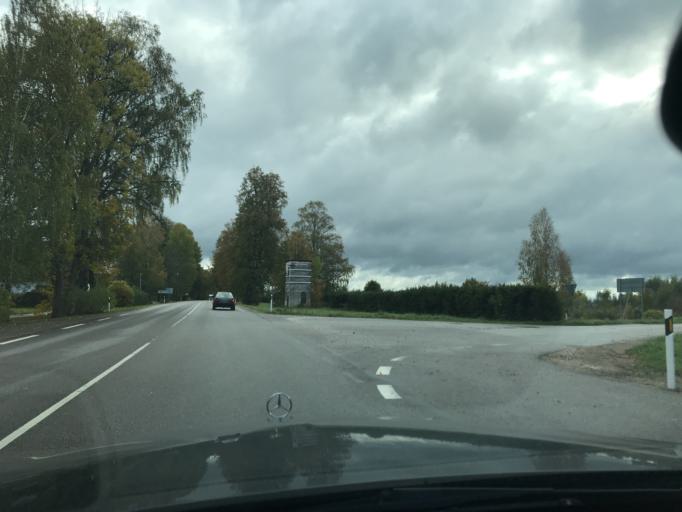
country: EE
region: Valgamaa
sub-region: Torva linn
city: Torva
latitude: 58.0141
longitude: 25.8818
